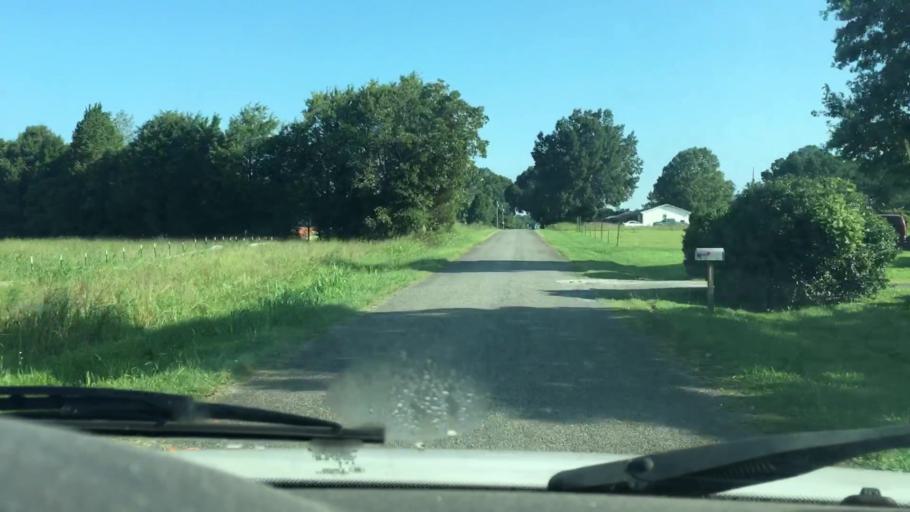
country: US
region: North Carolina
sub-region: Mecklenburg County
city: Huntersville
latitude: 35.4254
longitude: -80.8085
